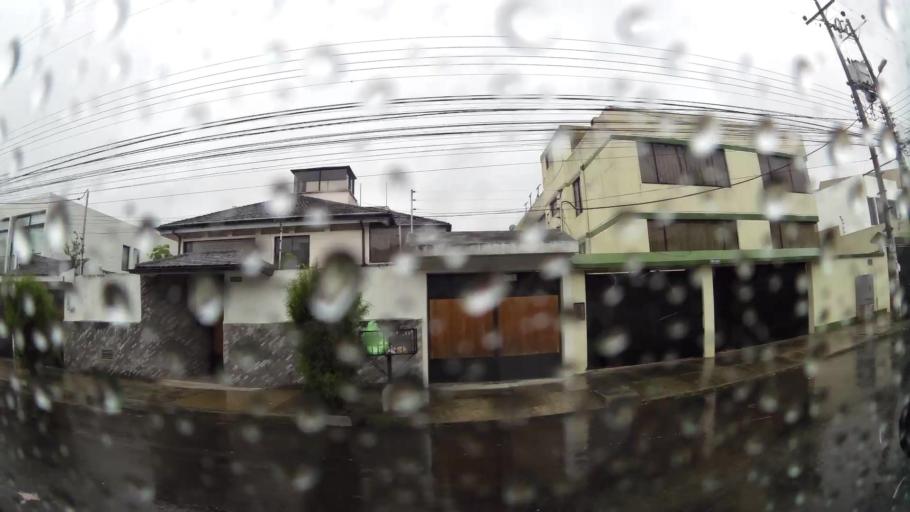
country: EC
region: Pichincha
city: Quito
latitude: -0.0990
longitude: -78.4978
